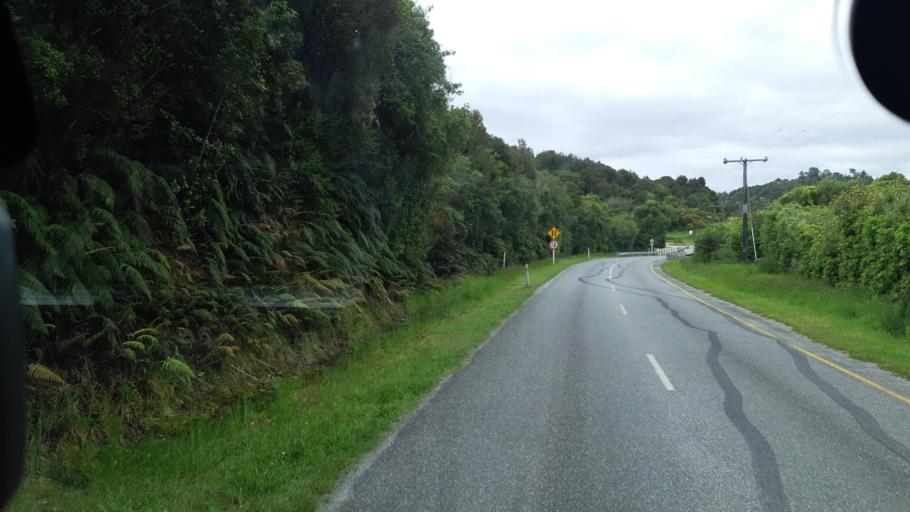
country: NZ
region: West Coast
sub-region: Westland District
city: Hokitika
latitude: -42.7638
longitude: 171.0651
